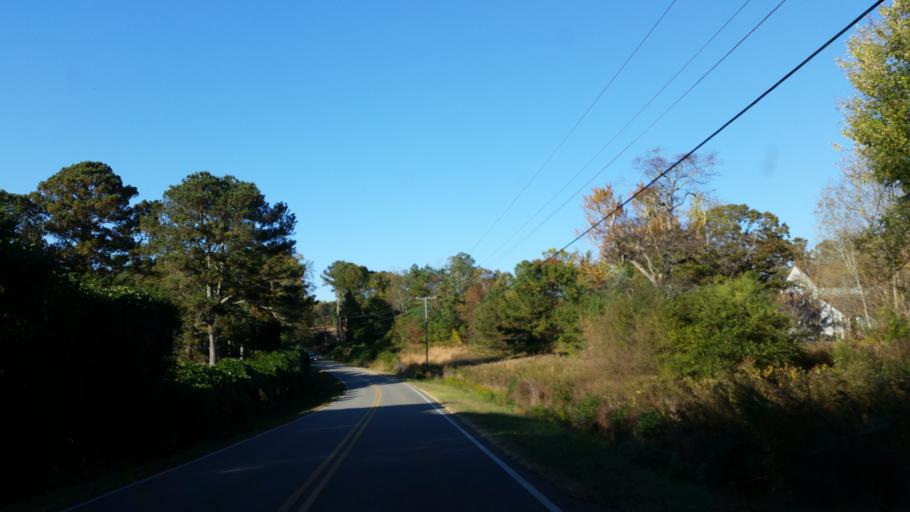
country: US
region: Georgia
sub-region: Pickens County
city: Jasper
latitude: 34.5769
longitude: -84.4576
